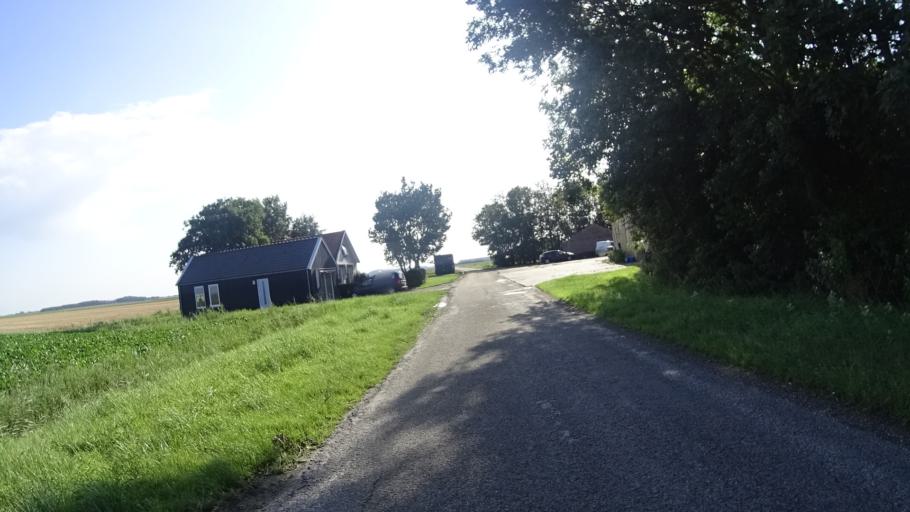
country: NL
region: Friesland
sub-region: Gemeente Harlingen
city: Harlingen
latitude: 53.1230
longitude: 5.4320
